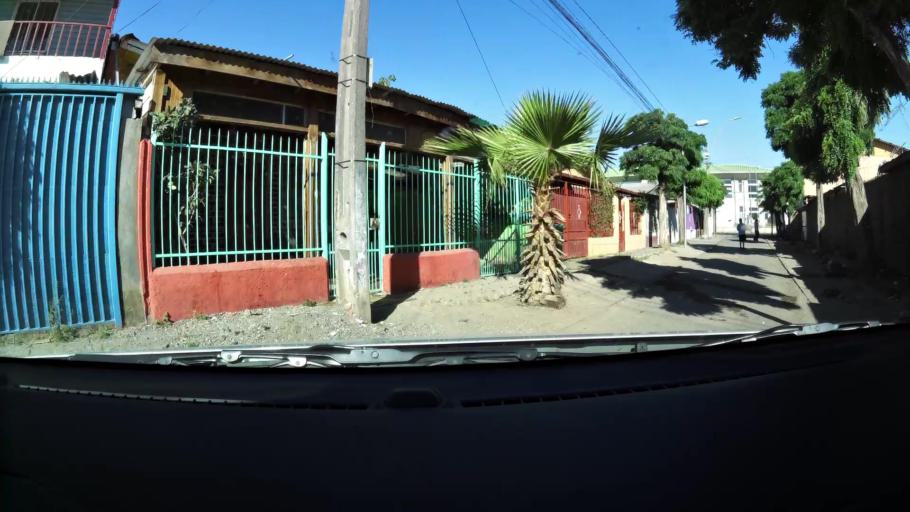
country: CL
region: Santiago Metropolitan
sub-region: Provincia de Maipo
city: San Bernardo
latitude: -33.5894
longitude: -70.6837
